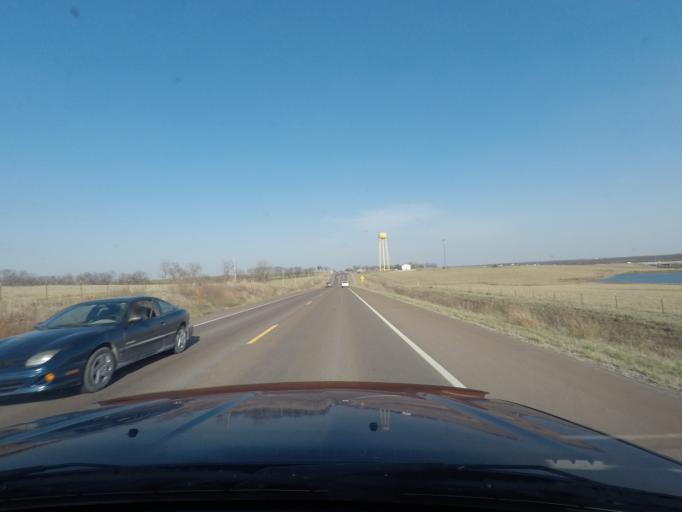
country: US
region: Kansas
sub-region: Douglas County
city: Lawrence
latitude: 39.0004
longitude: -95.3491
